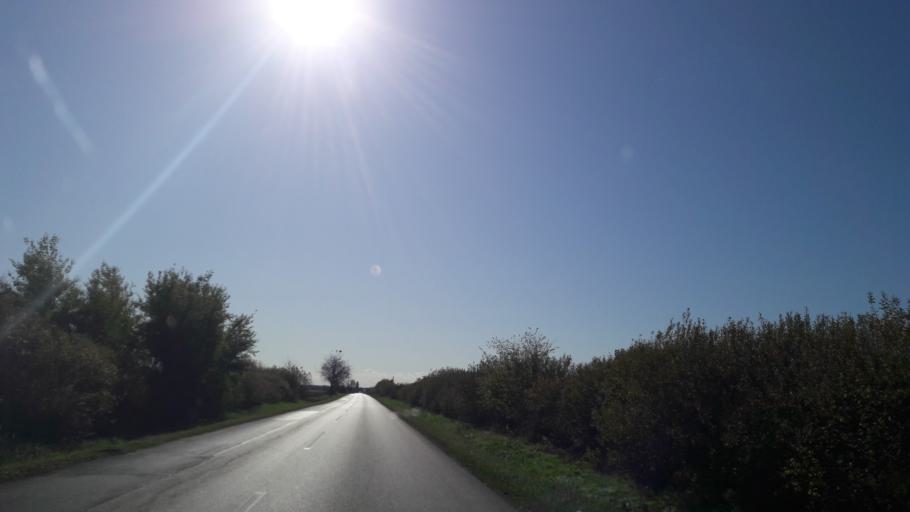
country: HR
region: Osjecko-Baranjska
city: Gorjani
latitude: 45.3733
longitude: 18.3715
